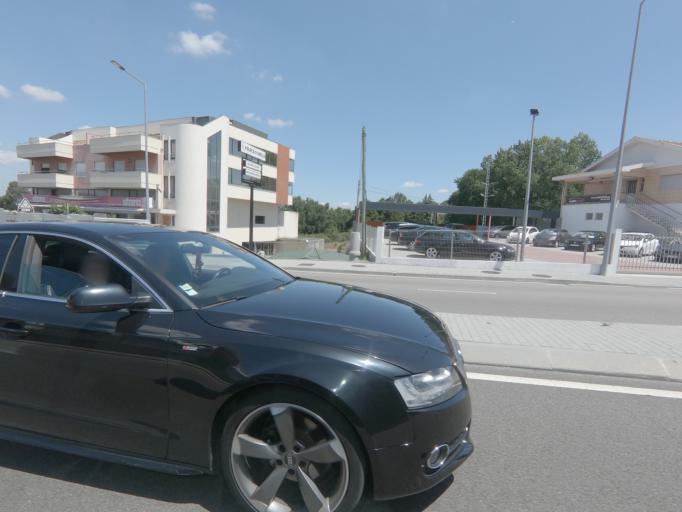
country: PT
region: Porto
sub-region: Penafiel
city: Penafiel
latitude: 41.1941
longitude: -8.3054
